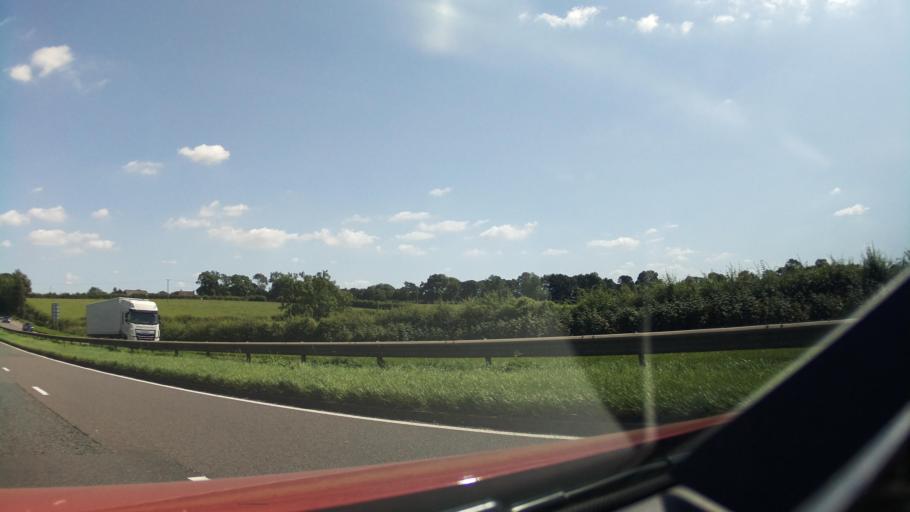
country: GB
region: England
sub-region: Warwickshire
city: Atherstone
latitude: 52.5864
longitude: -1.5771
